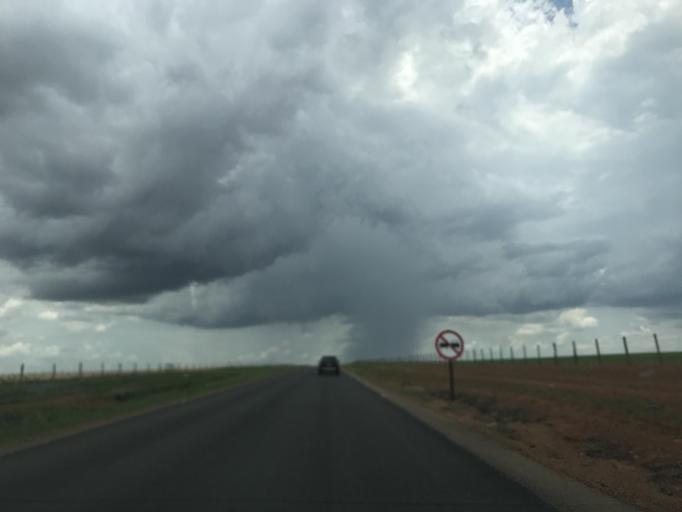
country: BR
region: Goias
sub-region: Vianopolis
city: Vianopolis
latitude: -16.8224
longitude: -48.5266
